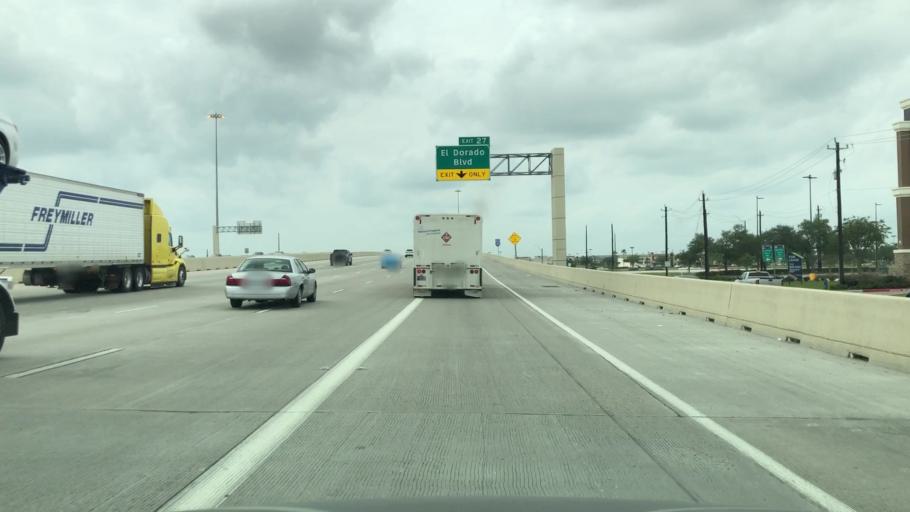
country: US
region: Texas
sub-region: Harris County
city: Webster
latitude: 29.5381
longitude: -95.1389
